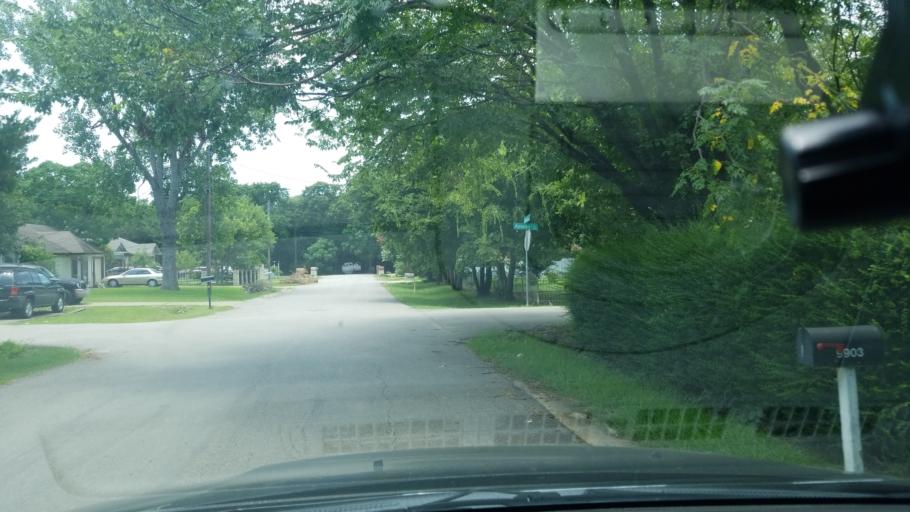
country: US
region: Texas
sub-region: Dallas County
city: Balch Springs
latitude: 32.7159
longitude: -96.6524
